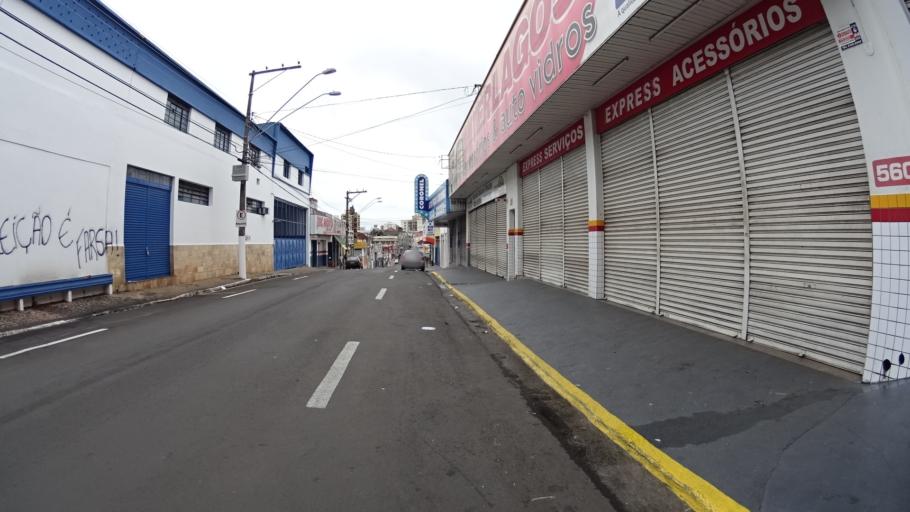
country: BR
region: Sao Paulo
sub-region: Marilia
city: Marilia
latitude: -22.2211
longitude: -49.9532
